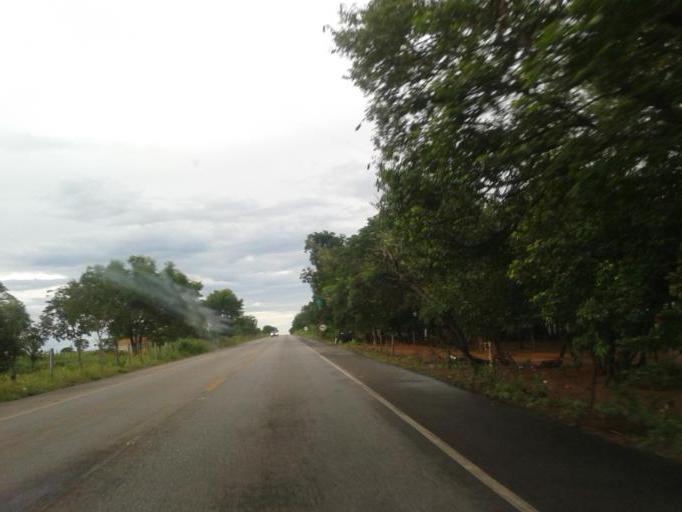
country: BR
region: Goias
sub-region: Mozarlandia
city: Mozarlandia
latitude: -14.7896
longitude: -50.5359
